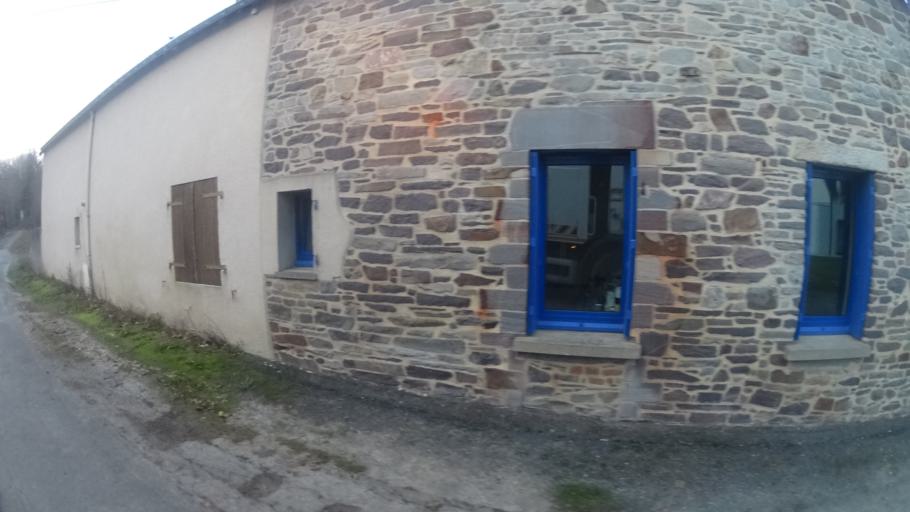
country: FR
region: Pays de la Loire
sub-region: Departement de la Loire-Atlantique
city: Saint-Nicolas-de-Redon
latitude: 47.6469
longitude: -2.0612
